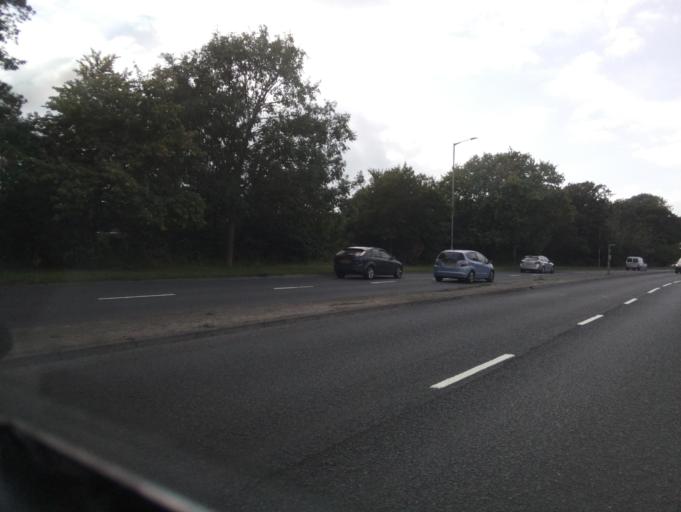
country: GB
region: England
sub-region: Hampshire
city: Bransgore
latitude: 50.7422
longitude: -1.7385
